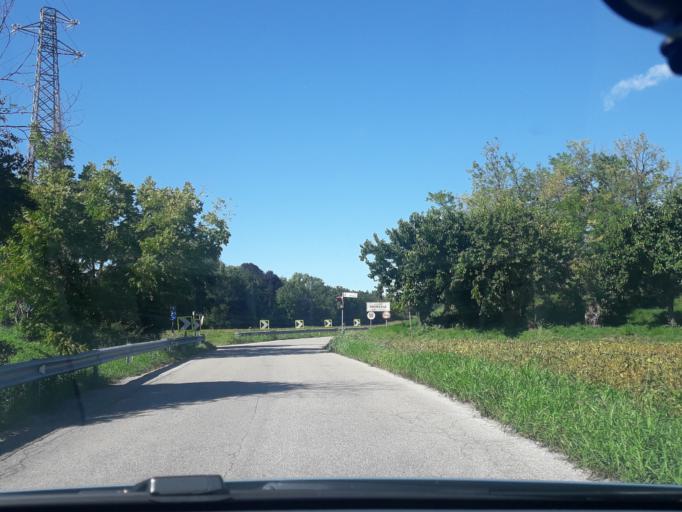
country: IT
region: Friuli Venezia Giulia
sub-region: Provincia di Udine
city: Reana del Roiale
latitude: 46.1384
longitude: 13.2162
